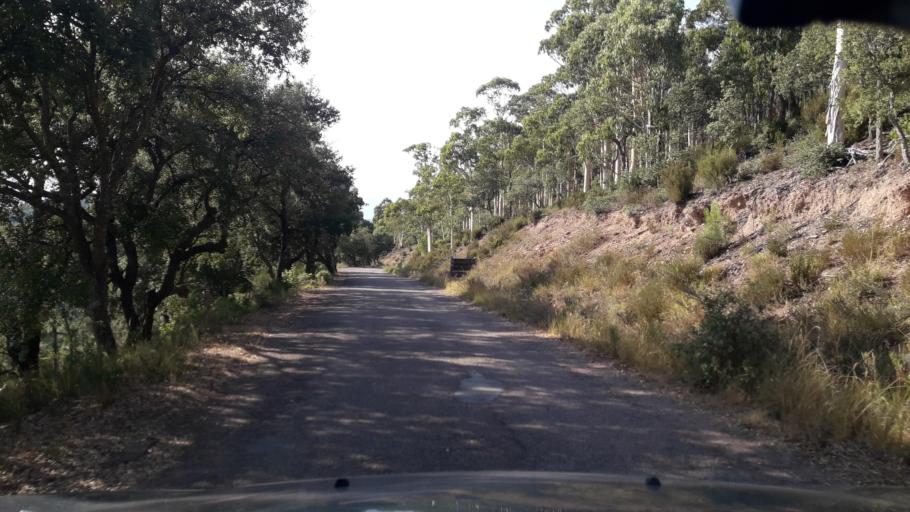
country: FR
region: Provence-Alpes-Cote d'Azur
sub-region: Departement du Var
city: Saint-Raphael
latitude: 43.4968
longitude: 6.8014
